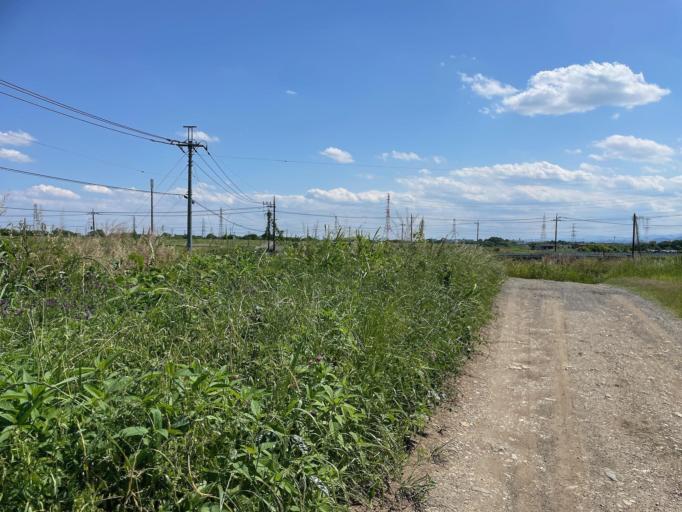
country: JP
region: Saitama
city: Sakado
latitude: 35.9957
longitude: 139.4093
